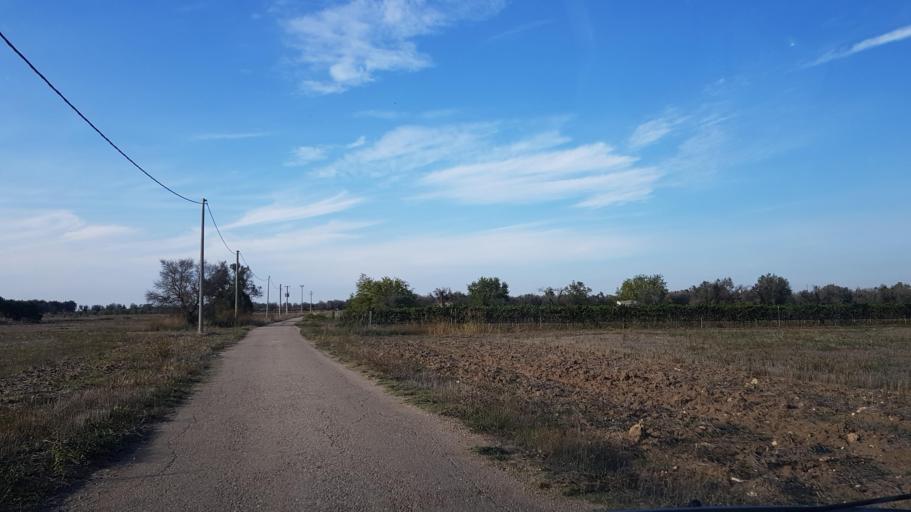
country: IT
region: Apulia
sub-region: Provincia di Brindisi
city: Mesagne
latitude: 40.5002
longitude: 17.8505
